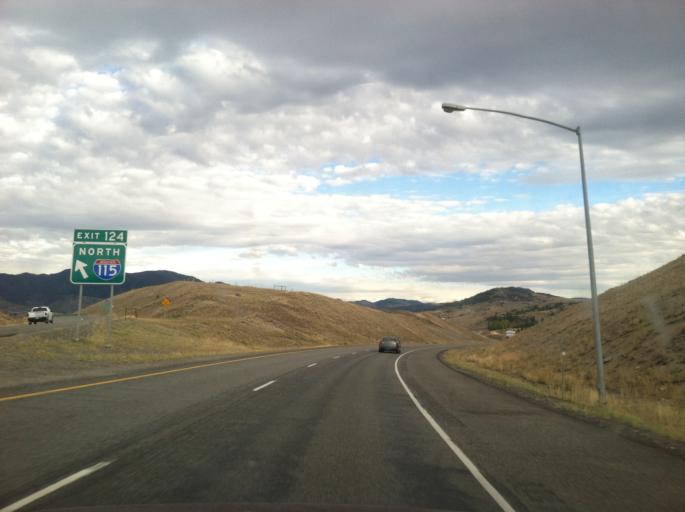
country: US
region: Montana
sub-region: Silver Bow County
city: Butte
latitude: 46.0041
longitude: -112.5729
